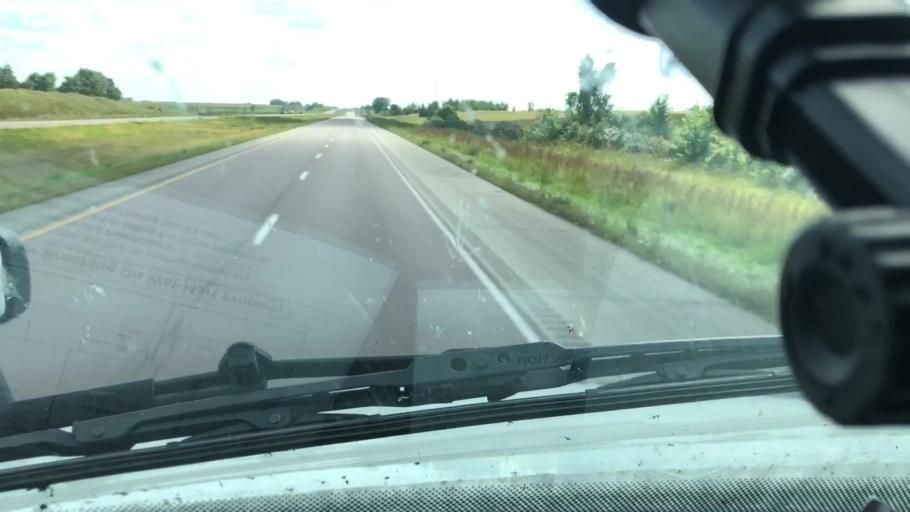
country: US
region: Iowa
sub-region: Worth County
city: Manly
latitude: 43.3098
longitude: -93.3492
